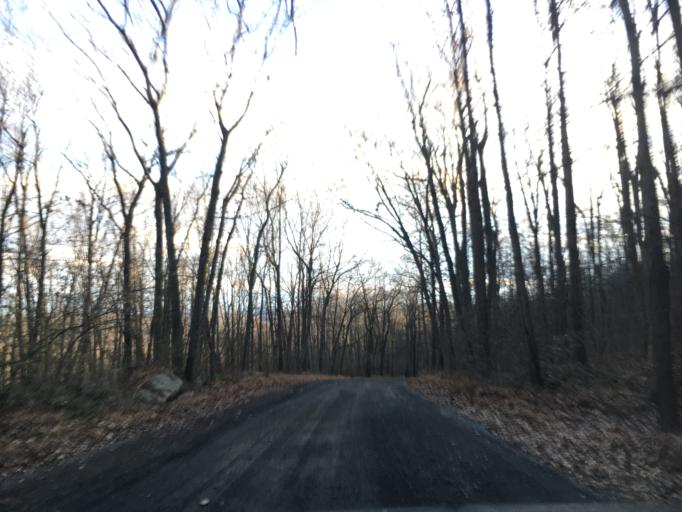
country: US
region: Pennsylvania
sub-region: Carbon County
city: Lehighton
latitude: 40.7653
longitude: -75.6954
